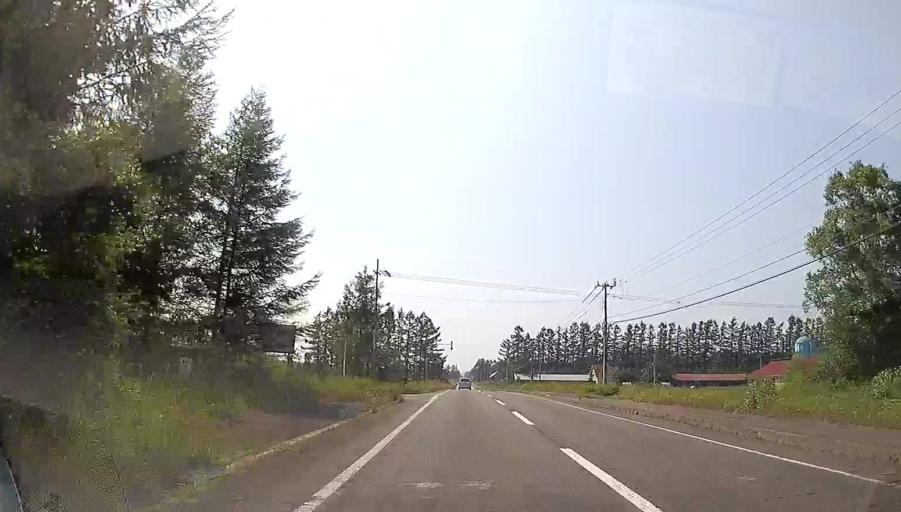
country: JP
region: Hokkaido
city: Otofuke
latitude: 43.1715
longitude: 143.1047
